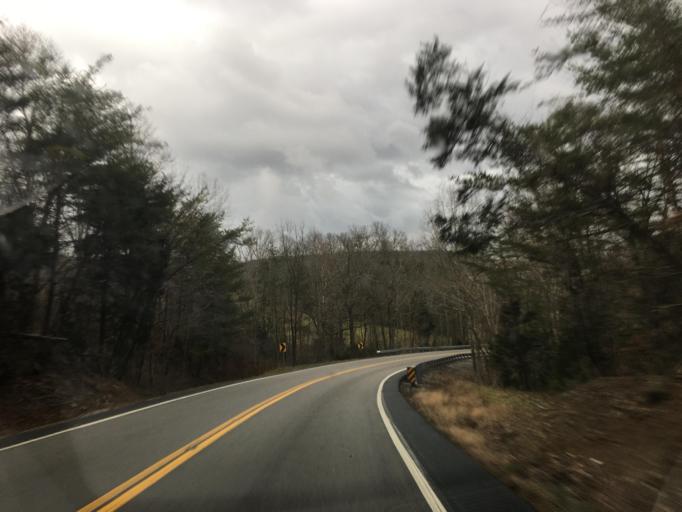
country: US
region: Tennessee
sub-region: Cumberland County
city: Lake Tansi
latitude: 35.8673
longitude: -84.9223
